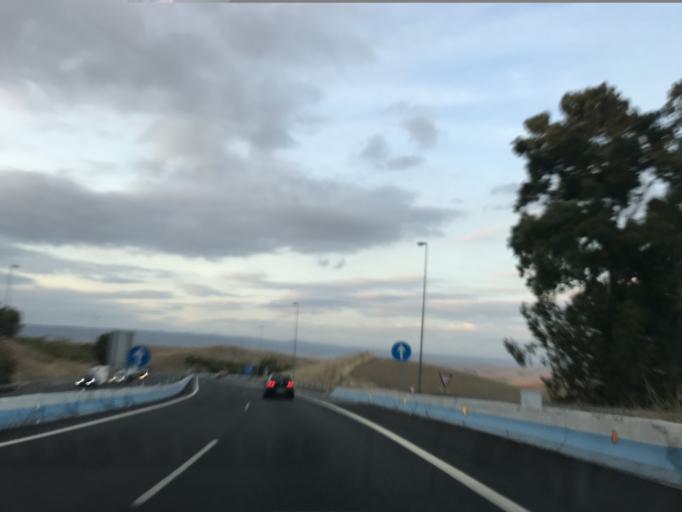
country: ES
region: Andalusia
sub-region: Province of Cordoba
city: La Victoria
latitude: 37.7623
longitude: -4.8226
